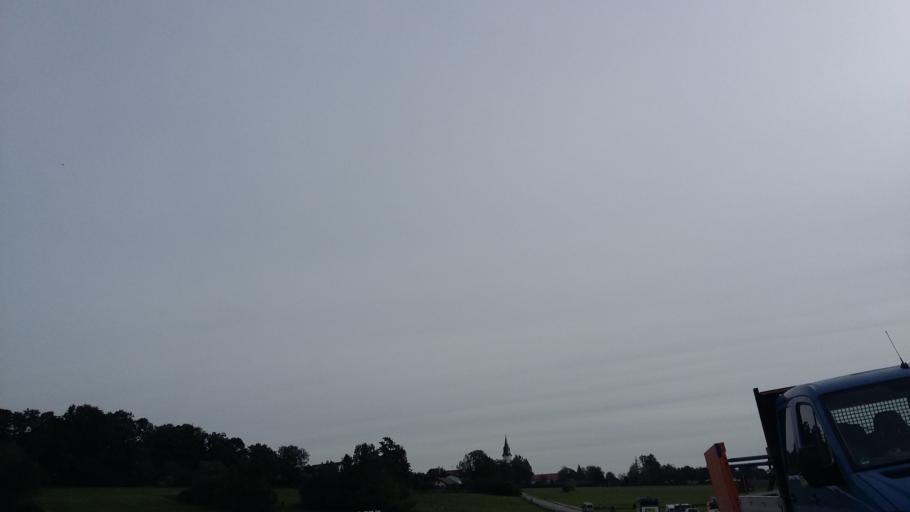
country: DE
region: Bavaria
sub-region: Upper Bavaria
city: Berg
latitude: 47.9625
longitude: 11.3596
